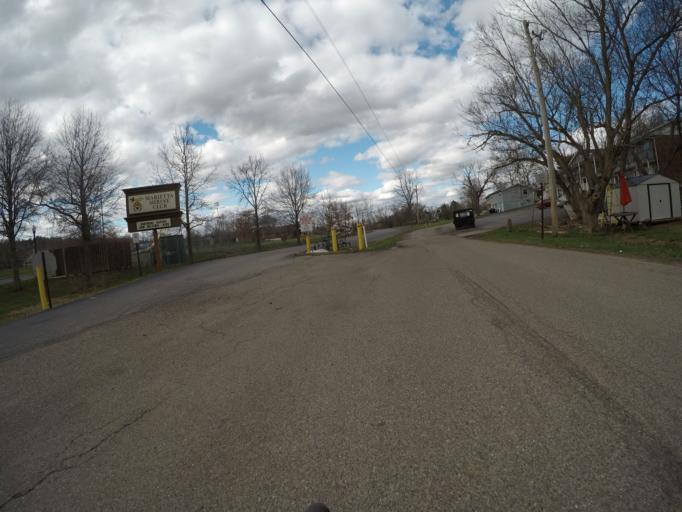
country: US
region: Ohio
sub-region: Washington County
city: Marietta
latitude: 39.4342
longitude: -81.4662
